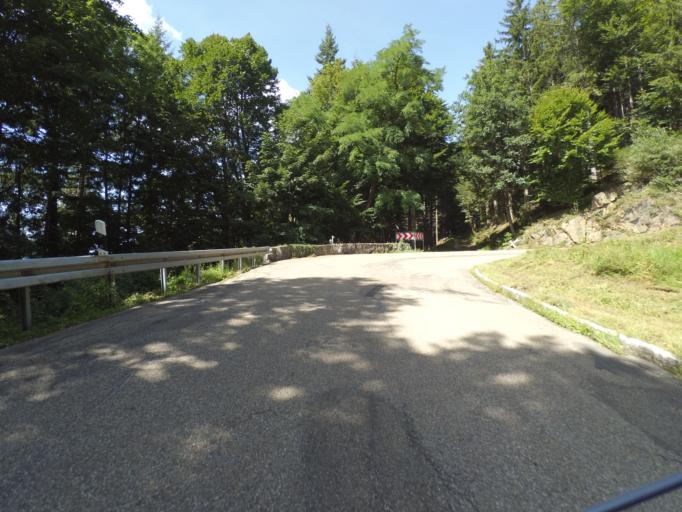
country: DE
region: Baden-Wuerttemberg
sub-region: Freiburg Region
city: Gutach im Breisgau
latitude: 48.0847
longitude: 7.9970
